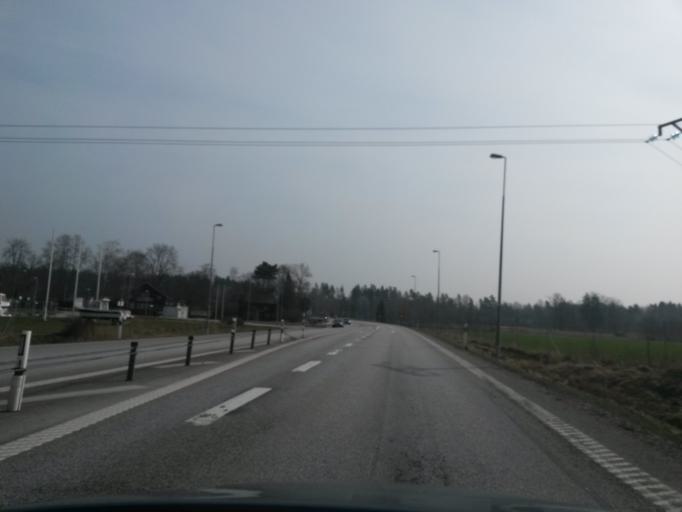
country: SE
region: Vaestra Goetaland
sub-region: Toreboda Kommun
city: Toereboda
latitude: 58.7987
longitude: 14.0532
